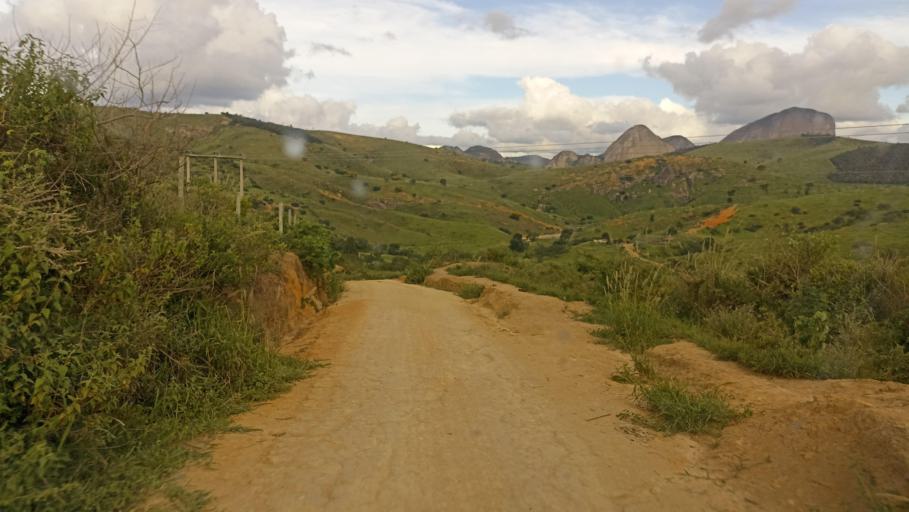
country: BR
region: Minas Gerais
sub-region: Almenara
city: Almenara
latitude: -16.5388
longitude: -40.4451
